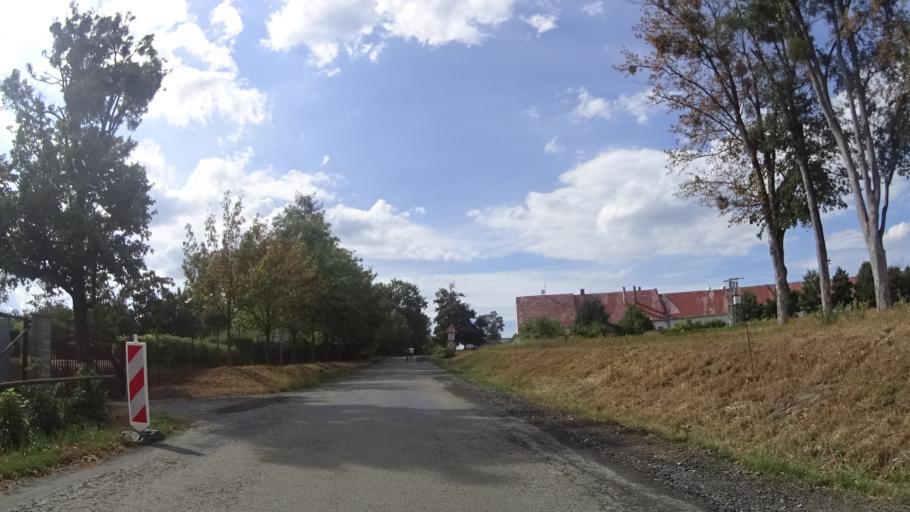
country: CZ
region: Olomoucky
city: Cervenka
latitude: 49.7210
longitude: 17.0311
